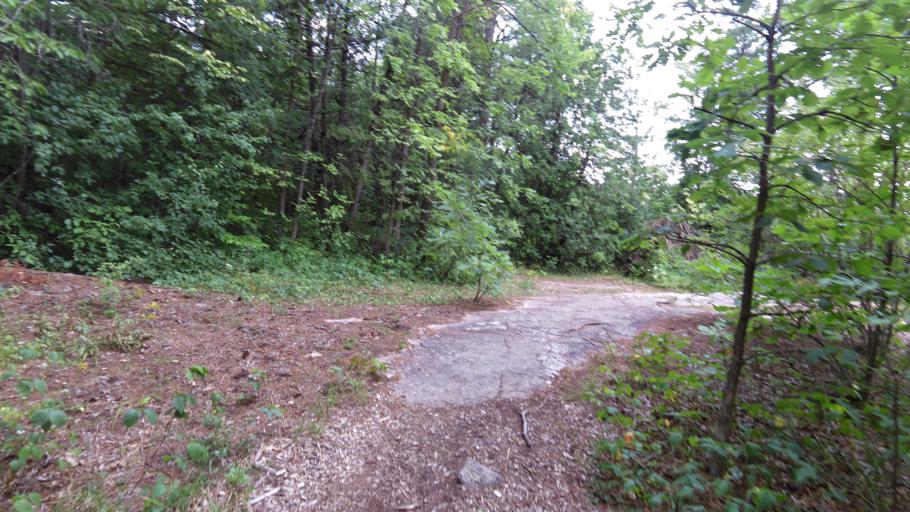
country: CA
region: Ontario
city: Carleton Place
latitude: 45.2682
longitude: -76.2499
